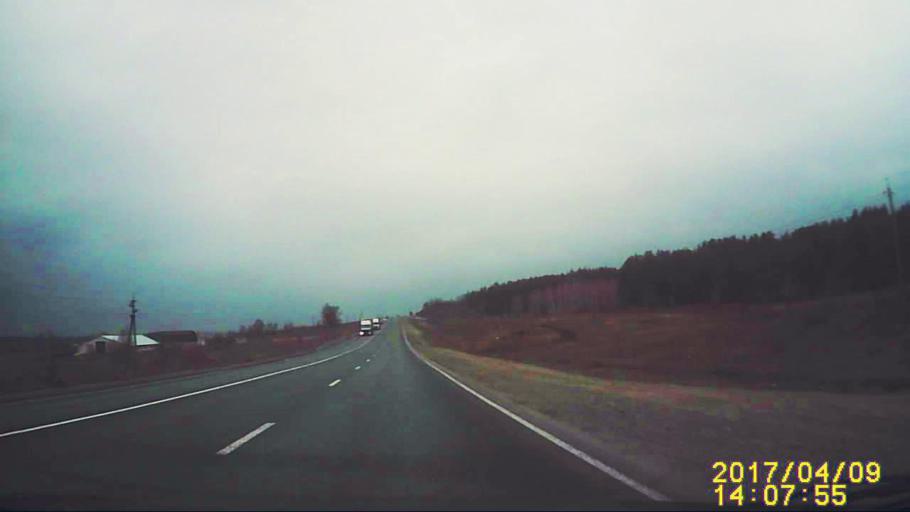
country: RU
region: Ulyanovsk
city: Silikatnyy
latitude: 54.0157
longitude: 48.2168
